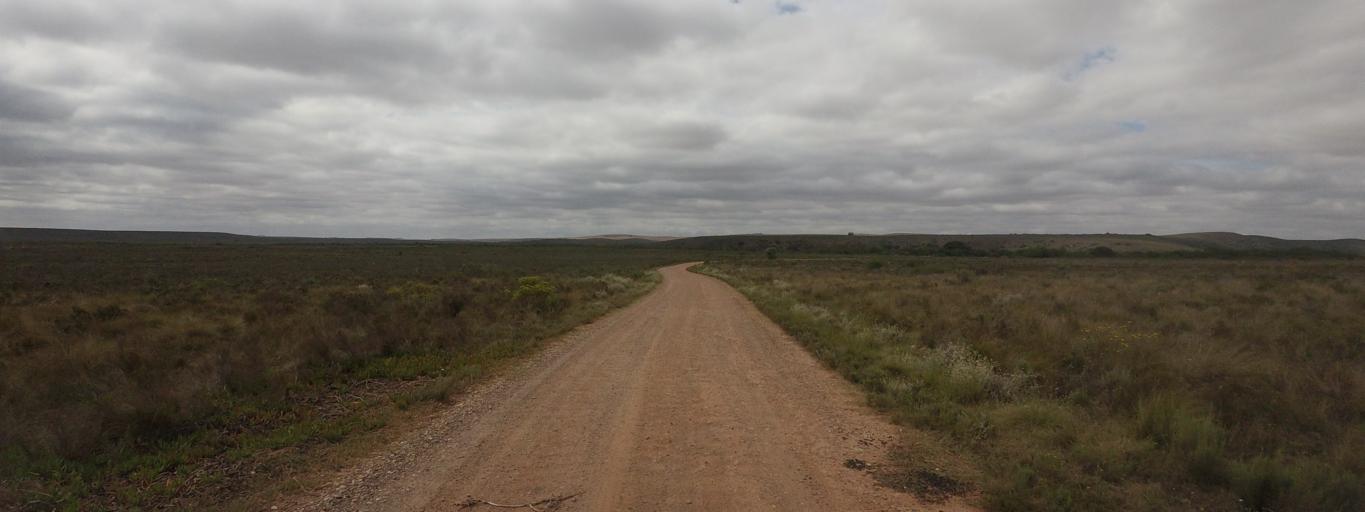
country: ZA
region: Western Cape
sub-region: Overberg District Municipality
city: Swellendam
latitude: -34.0627
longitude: 20.4383
